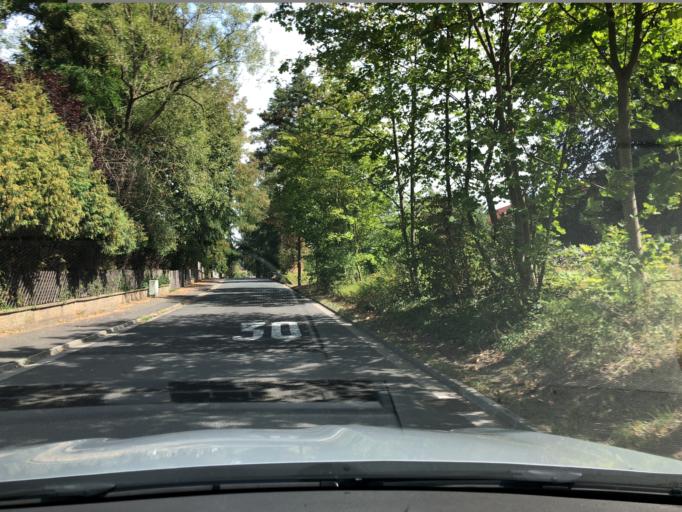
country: DE
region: Bavaria
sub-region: Regierungsbezirk Mittelfranken
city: Ruckersdorf
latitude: 49.4972
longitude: 11.2445
